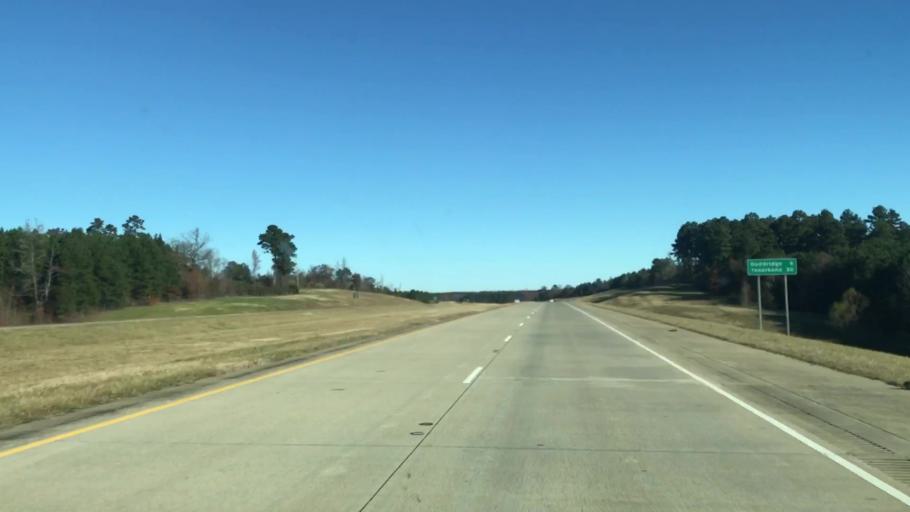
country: US
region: Louisiana
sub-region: Caddo Parish
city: Vivian
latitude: 33.0110
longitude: -93.9037
